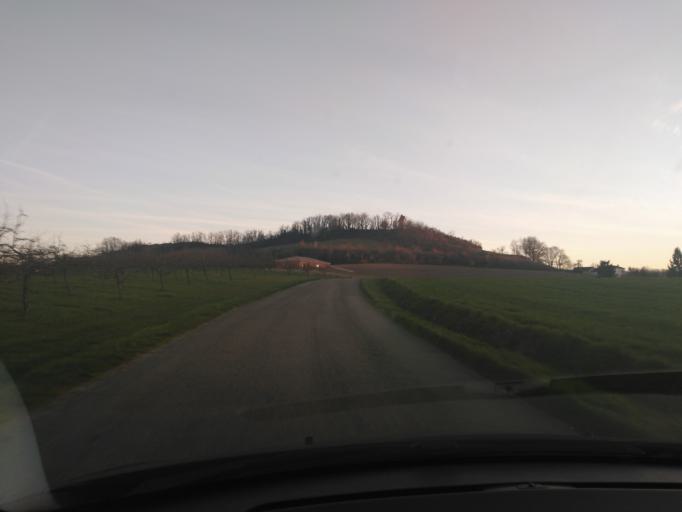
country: FR
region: Aquitaine
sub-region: Departement du Lot-et-Garonne
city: Saint-Hilaire
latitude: 44.5235
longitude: 0.6875
